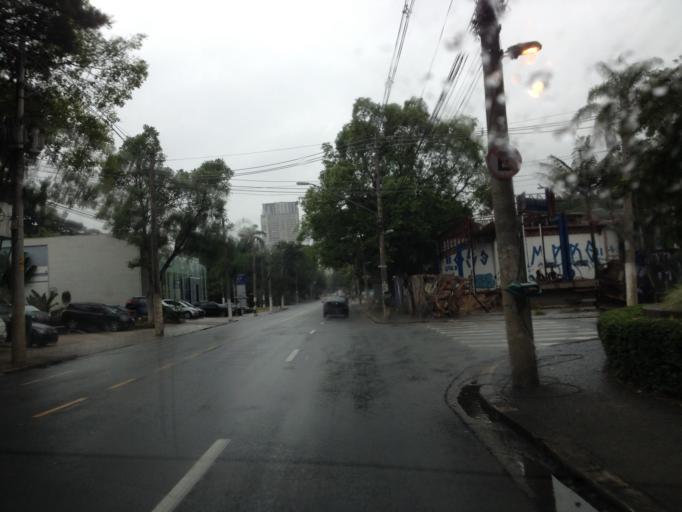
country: BR
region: Sao Paulo
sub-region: Sao Paulo
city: Sao Paulo
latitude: -23.5715
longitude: -46.6742
